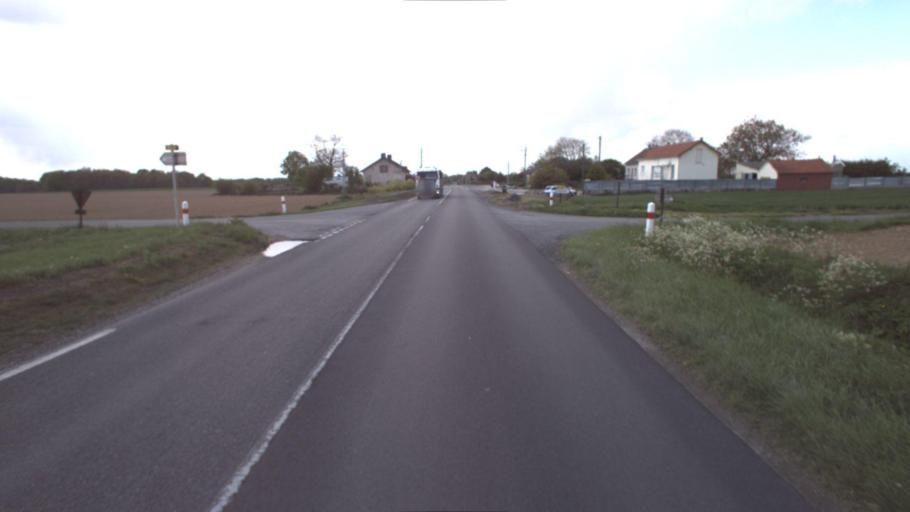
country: FR
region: Ile-de-France
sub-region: Departement de Seine-et-Marne
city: Jouy-le-Chatel
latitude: 48.6926
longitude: 3.1866
